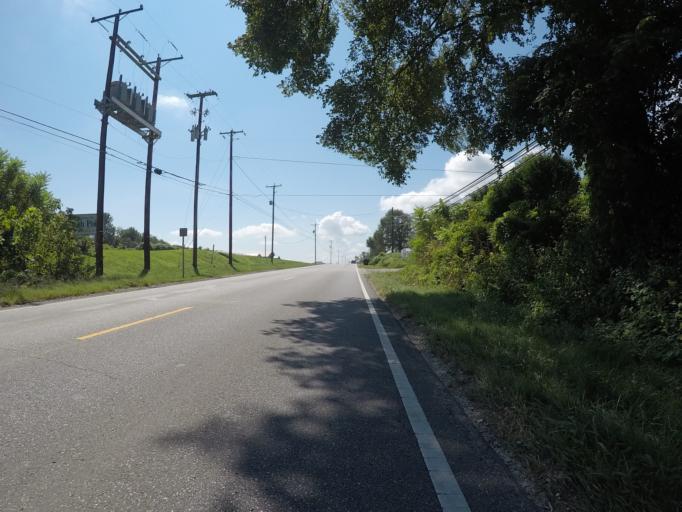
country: US
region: Ohio
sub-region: Lawrence County
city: South Point
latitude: 38.4443
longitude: -82.5942
